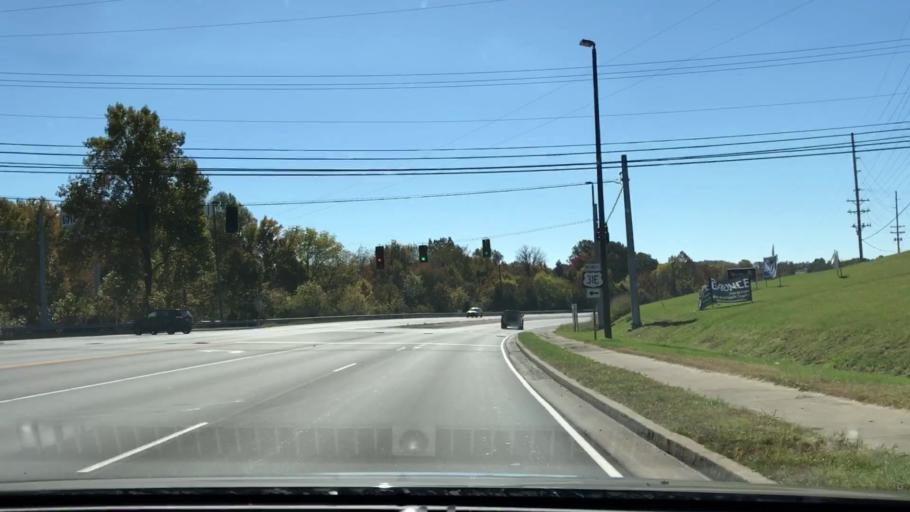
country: US
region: Kentucky
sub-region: Barren County
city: Glasgow
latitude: 36.9832
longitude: -85.9315
